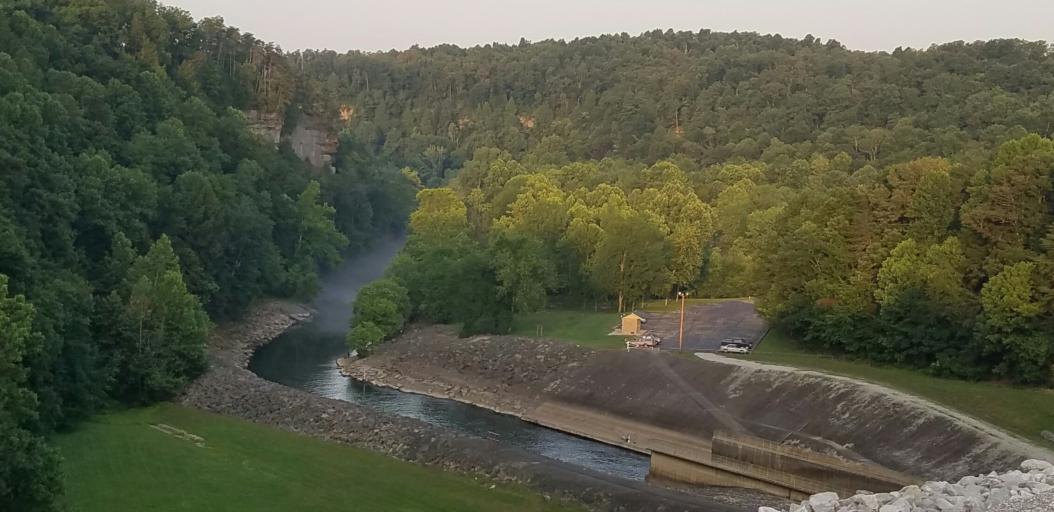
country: US
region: Kentucky
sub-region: Edmonson County
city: Brownsville
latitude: 37.2761
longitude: -86.2472
